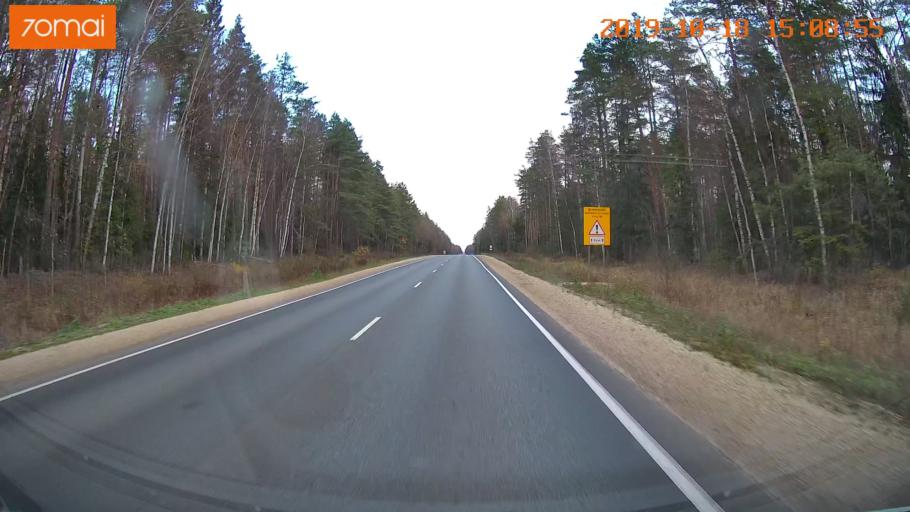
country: RU
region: Vladimir
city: Gus'-Khrustal'nyy
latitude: 55.5589
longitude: 40.6155
